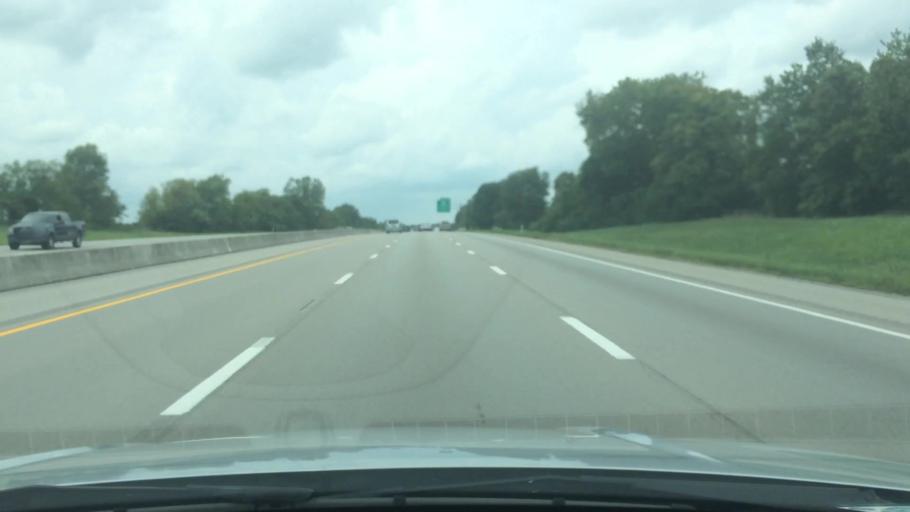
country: US
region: Kentucky
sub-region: Fayette County
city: Lexington
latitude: 37.9414
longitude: -84.3807
